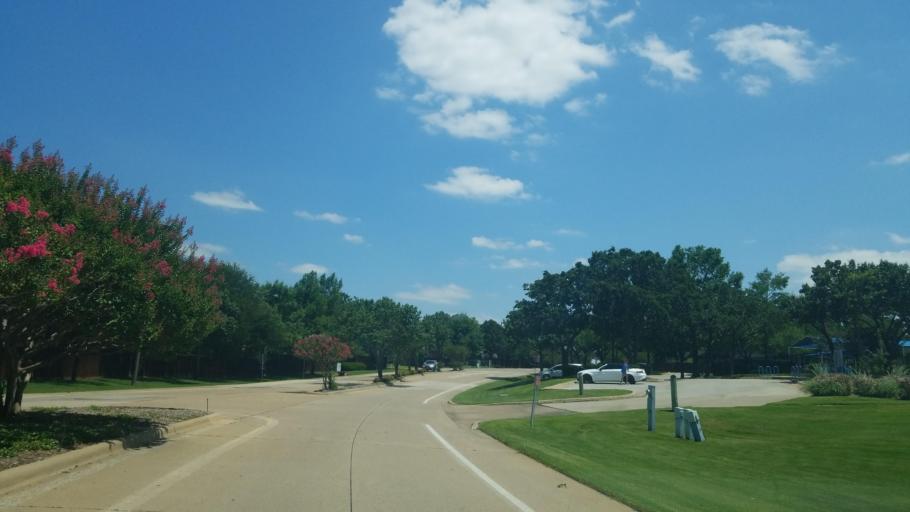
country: US
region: Texas
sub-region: Denton County
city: Highland Village
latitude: 33.0894
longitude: -97.0695
